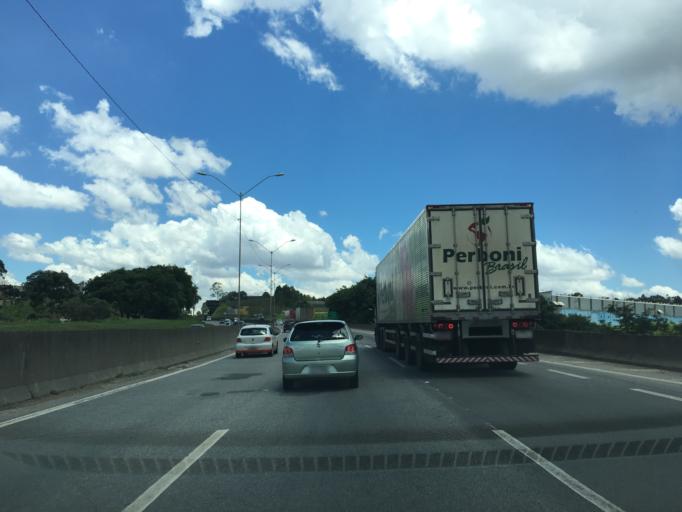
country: BR
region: Sao Paulo
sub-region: Guarulhos
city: Guarulhos
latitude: -23.4126
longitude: -46.5817
